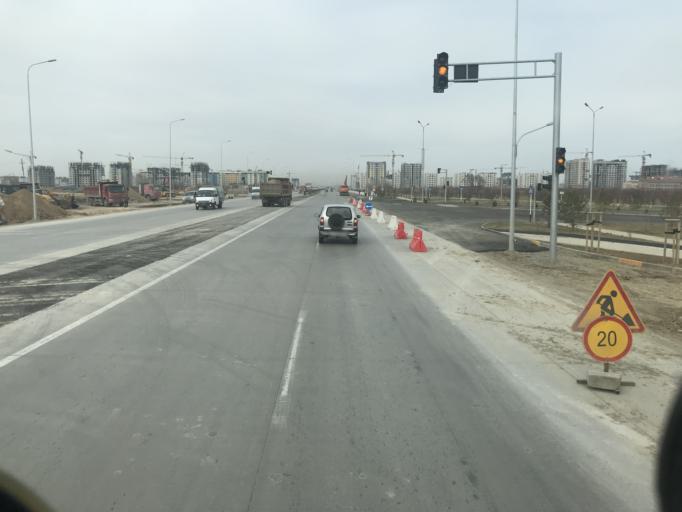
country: KZ
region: Ongtustik Qazaqstan
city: Turkestan
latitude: 43.2674
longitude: 68.3581
